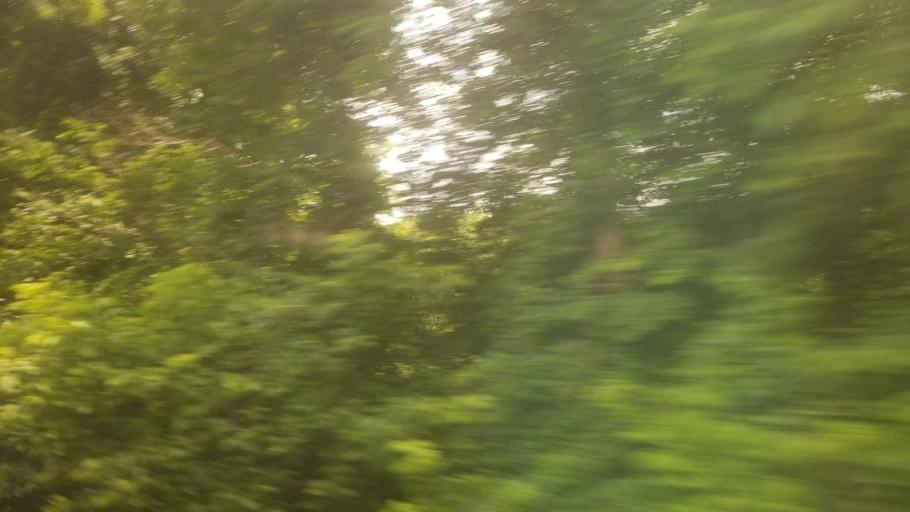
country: US
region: Maryland
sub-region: Montgomery County
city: Poolesville
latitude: 39.2198
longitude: -77.4199
